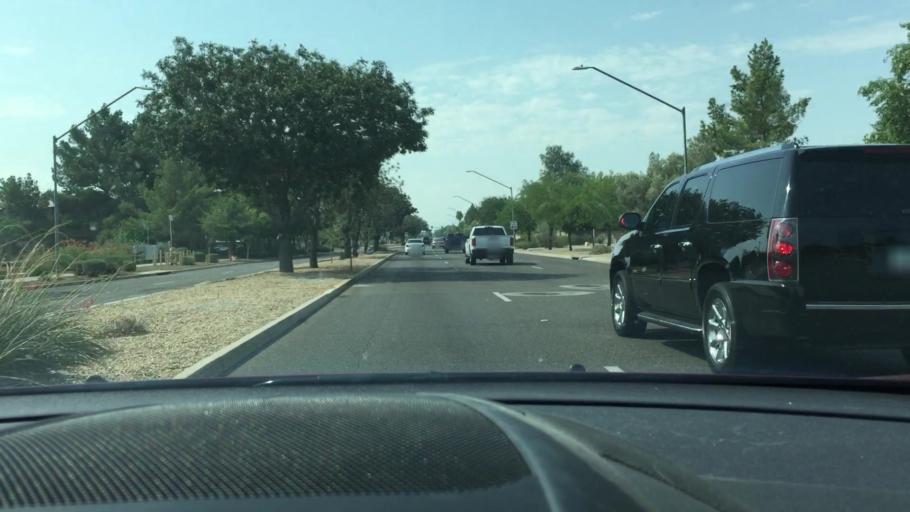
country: US
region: Arizona
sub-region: Maricopa County
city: Peoria
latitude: 33.6754
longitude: -112.2031
